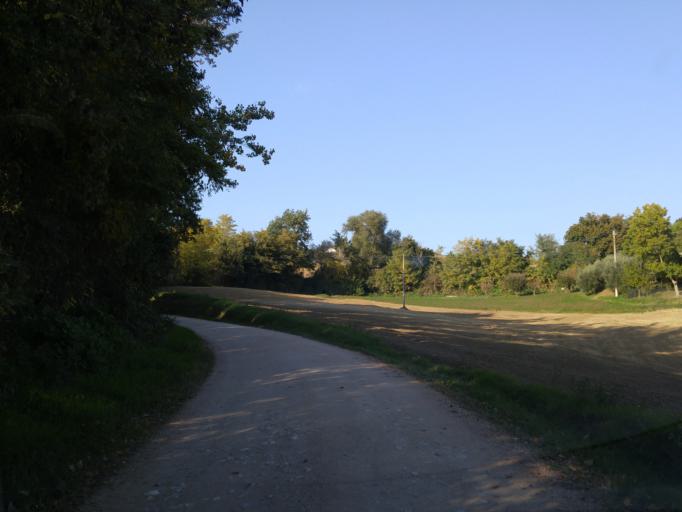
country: IT
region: The Marches
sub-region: Provincia di Pesaro e Urbino
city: Montefelcino
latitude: 43.7245
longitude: 12.8323
